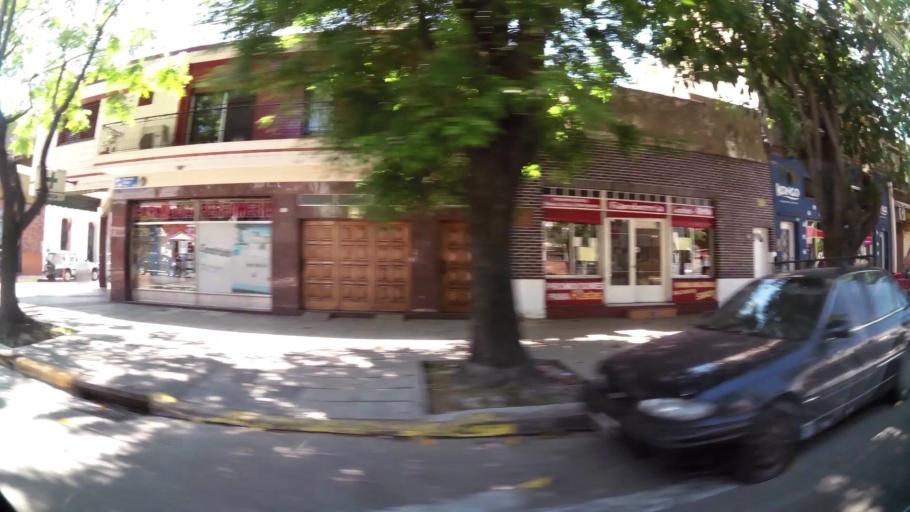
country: AR
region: Buenos Aires
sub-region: Partido de Avellaneda
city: Avellaneda
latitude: -34.6514
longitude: -58.3938
